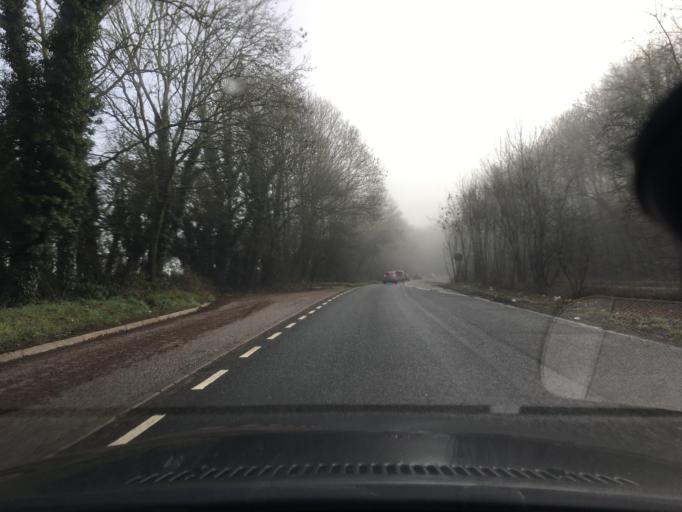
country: GB
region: England
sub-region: Hampshire
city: Old Basing
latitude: 51.2637
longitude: -1.0586
